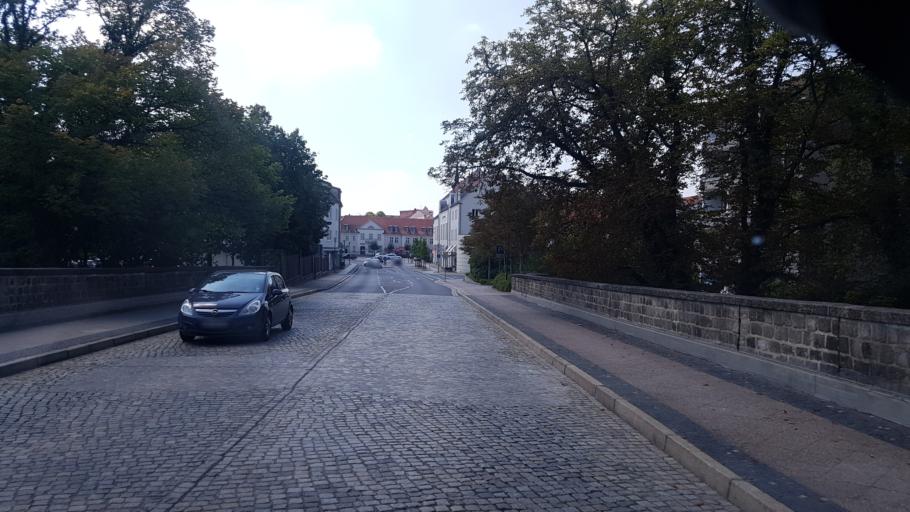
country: DE
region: Brandenburg
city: Spremberg
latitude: 51.5720
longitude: 14.3821
